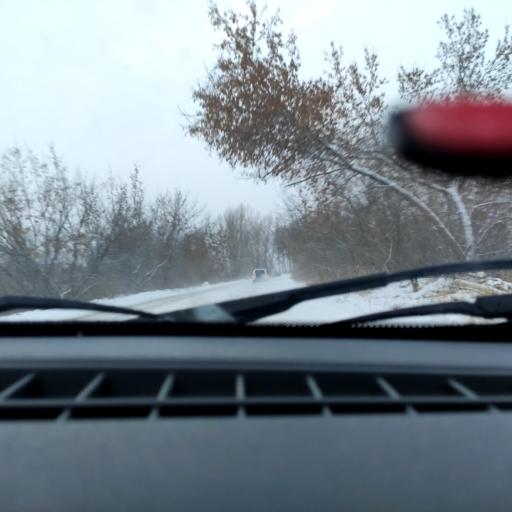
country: RU
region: Bashkortostan
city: Blagoveshchensk
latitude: 54.9084
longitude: 56.0075
